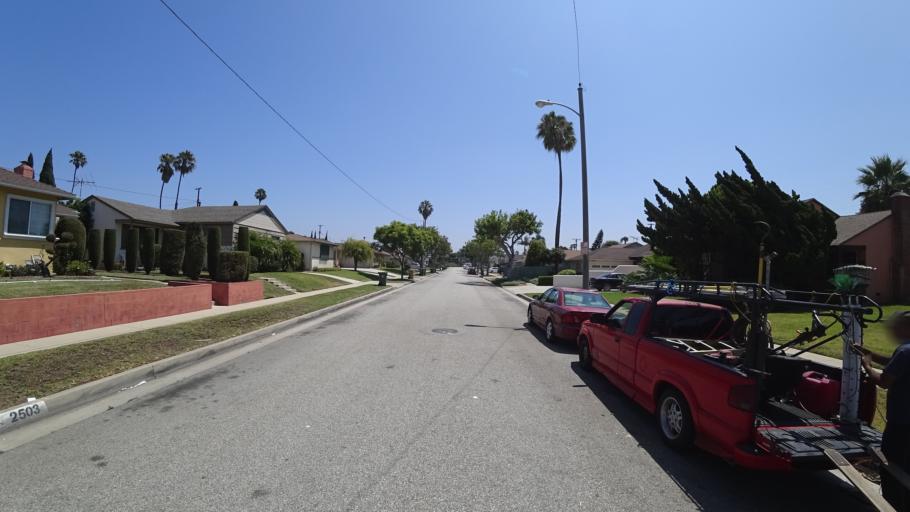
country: US
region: California
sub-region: Los Angeles County
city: West Athens
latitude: 33.9293
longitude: -118.3209
